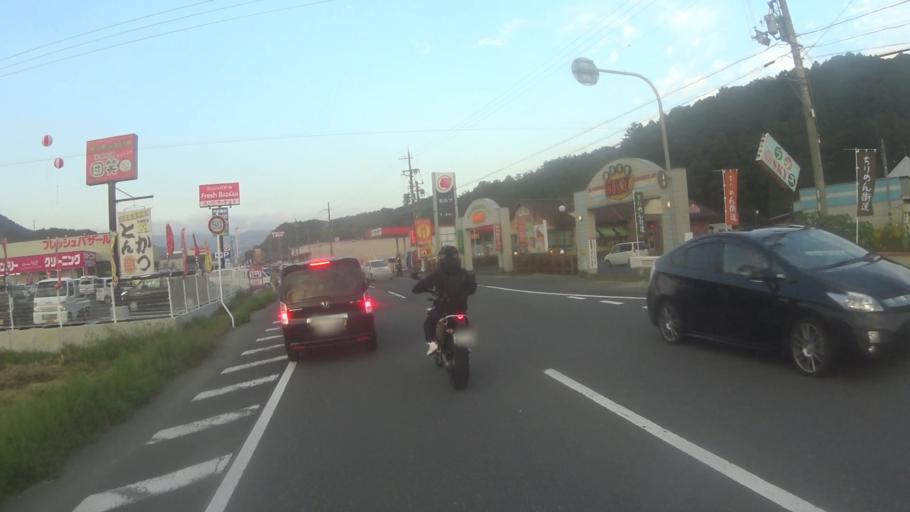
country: JP
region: Kyoto
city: Miyazu
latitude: 35.5394
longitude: 135.1301
